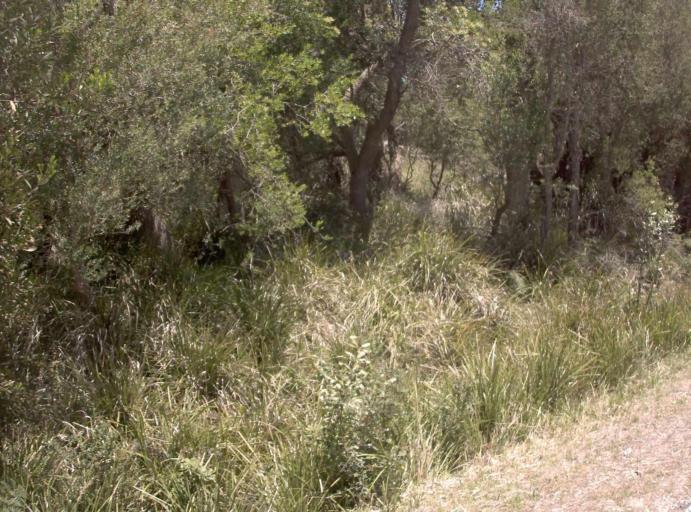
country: AU
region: Victoria
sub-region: Latrobe
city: Morwell
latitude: -38.8581
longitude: 146.2482
